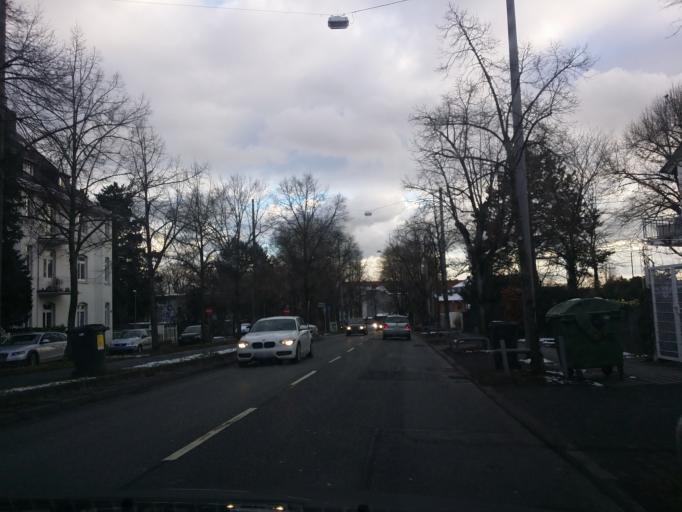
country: DE
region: Hesse
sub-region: Regierungsbezirk Darmstadt
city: Wiesbaden
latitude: 50.0955
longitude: 8.2214
